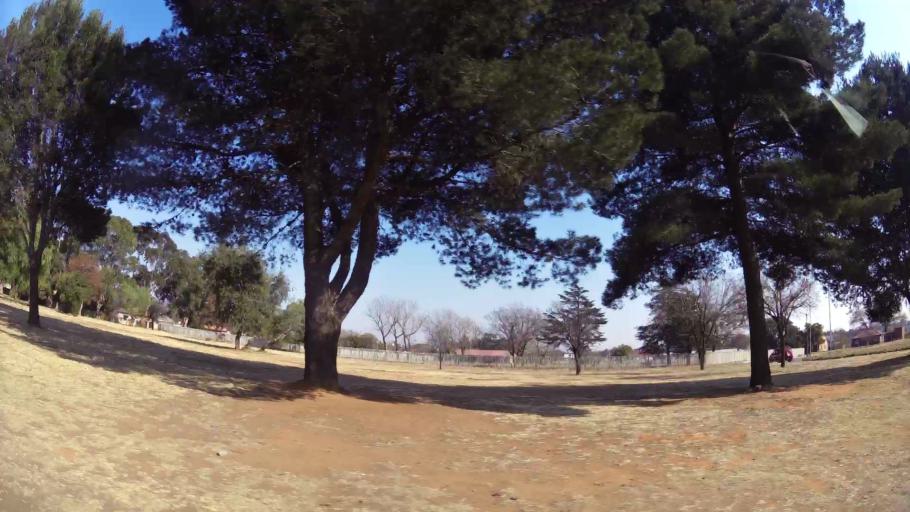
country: ZA
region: Gauteng
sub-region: Ekurhuleni Metropolitan Municipality
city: Boksburg
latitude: -26.2193
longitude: 28.2636
